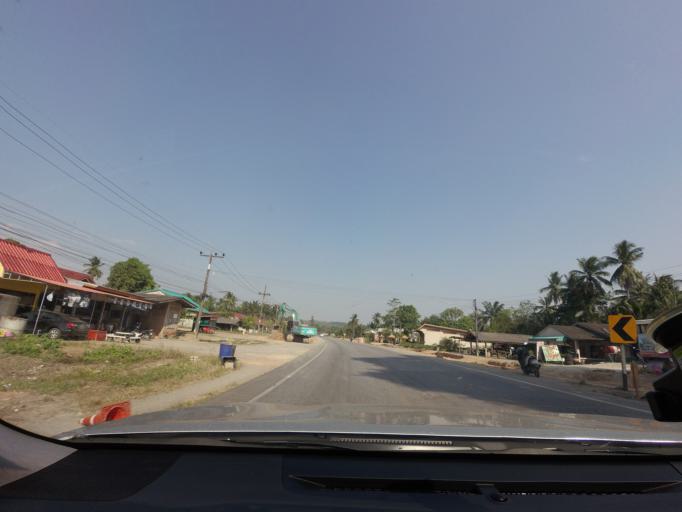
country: TH
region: Surat Thani
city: Chai Buri
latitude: 8.6026
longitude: 99.0100
